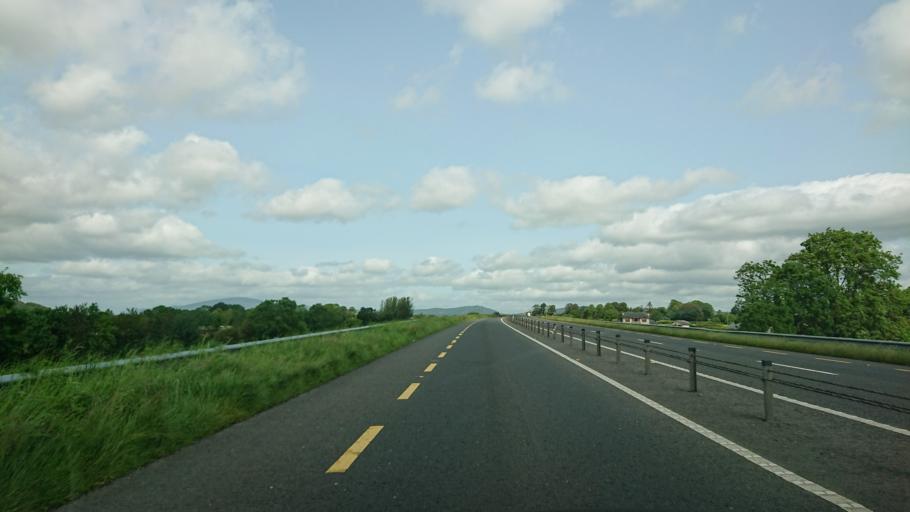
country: IE
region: Munster
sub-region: Waterford
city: Portlaw
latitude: 52.3233
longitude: -7.3029
